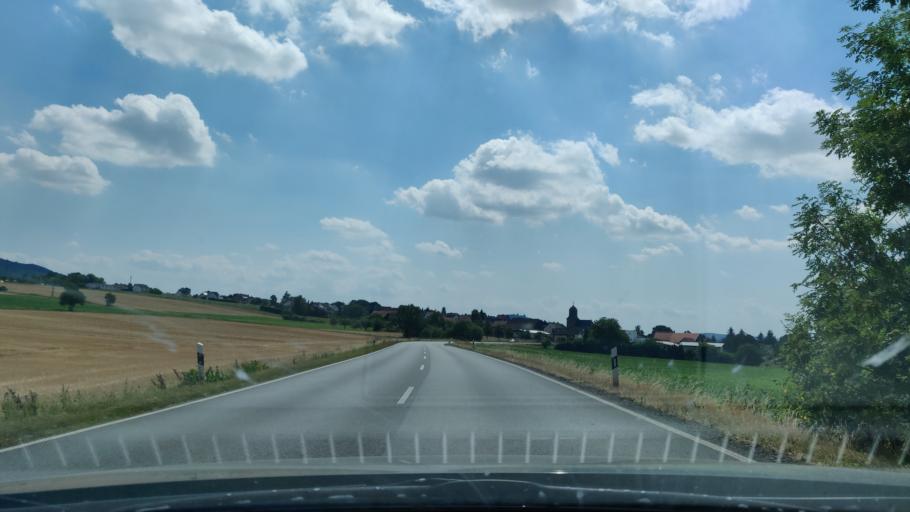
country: DE
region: Hesse
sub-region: Regierungsbezirk Kassel
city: Wabern
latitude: 51.0729
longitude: 9.3777
